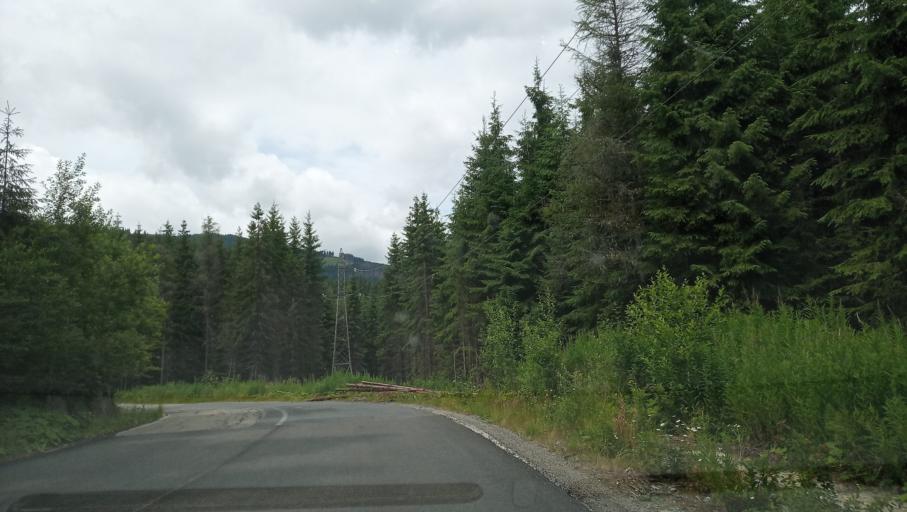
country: RO
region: Valcea
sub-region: Comuna Voineasa
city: Voineasa
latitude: 45.4155
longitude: 23.7280
